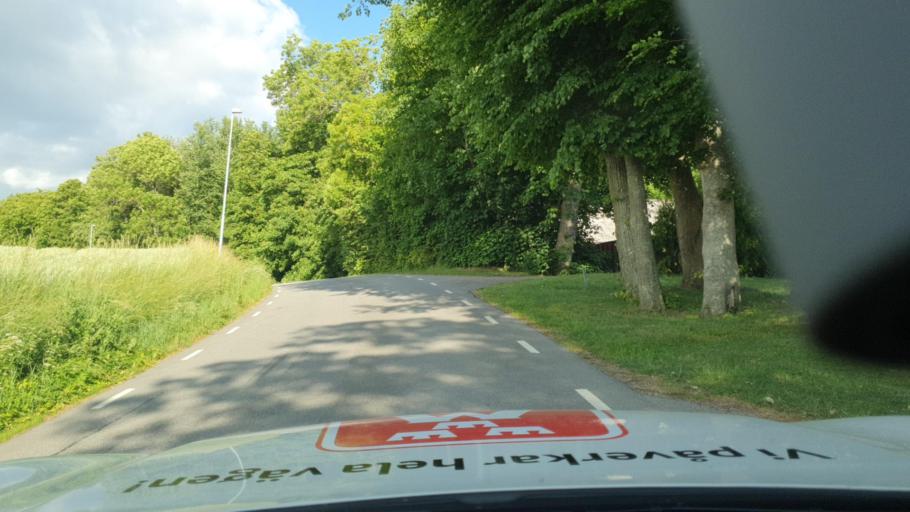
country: SE
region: Skane
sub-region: Ystads Kommun
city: Ystad
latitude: 55.4467
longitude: 13.7130
